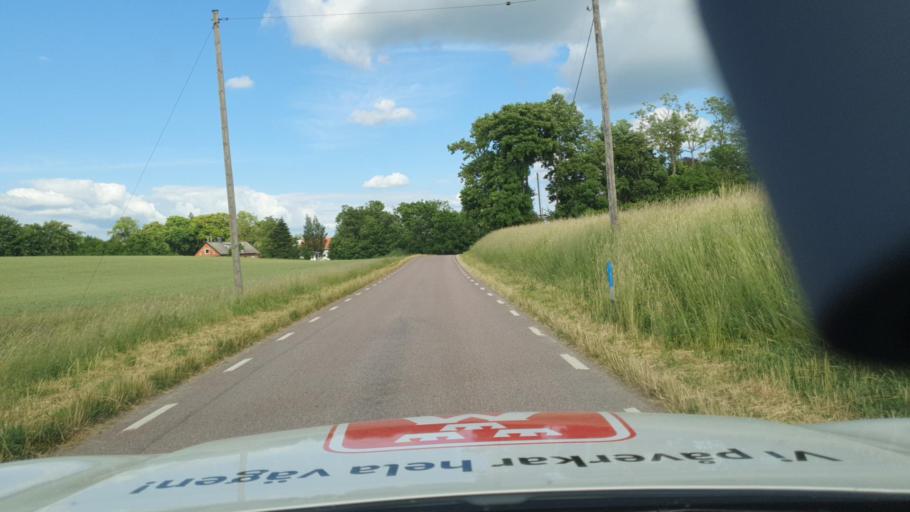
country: SE
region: Skane
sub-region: Skurups Kommun
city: Rydsgard
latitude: 55.4518
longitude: 13.5711
